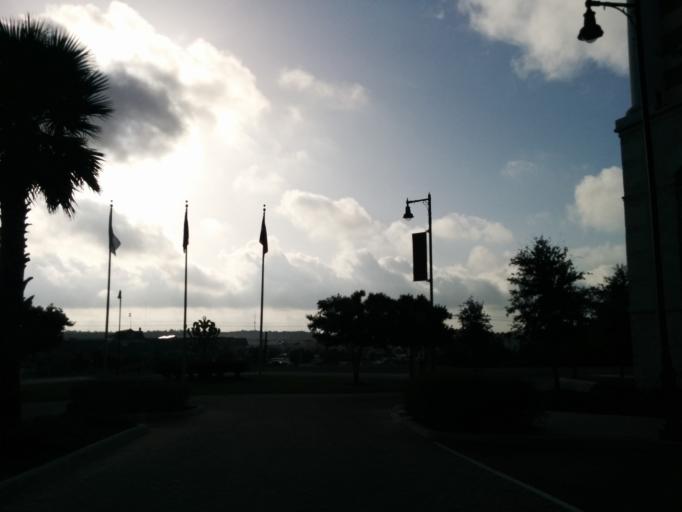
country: US
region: Texas
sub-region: Bexar County
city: Shavano Park
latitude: 29.6099
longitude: -98.6050
